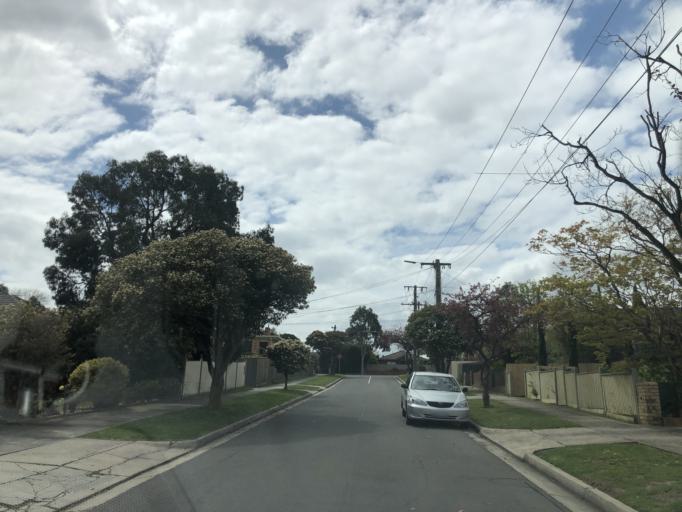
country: AU
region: Victoria
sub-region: Monash
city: Chadstone
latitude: -37.8827
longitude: 145.1037
